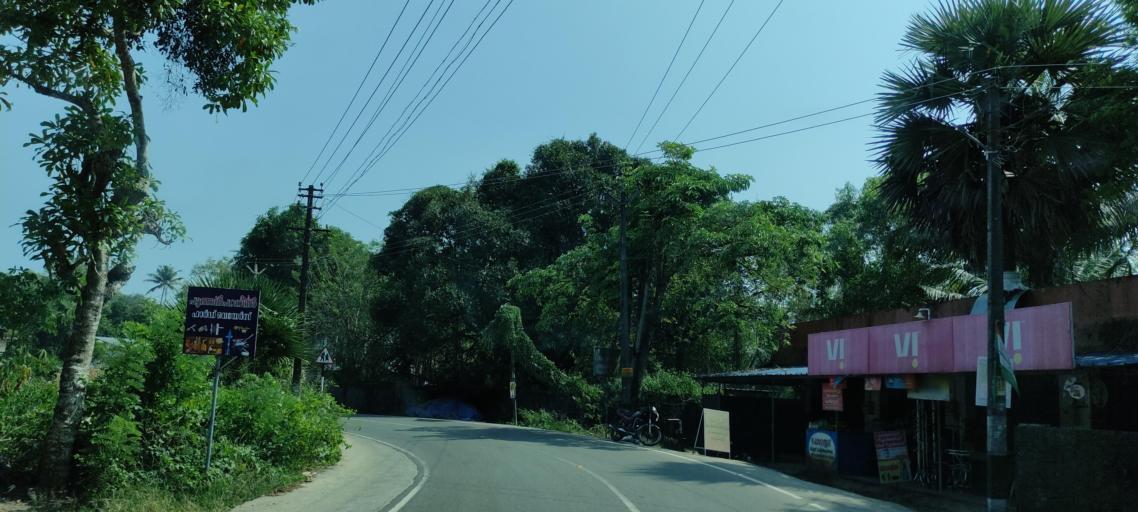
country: IN
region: Kerala
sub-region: Alappuzha
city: Shertallai
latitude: 9.6012
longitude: 76.3157
